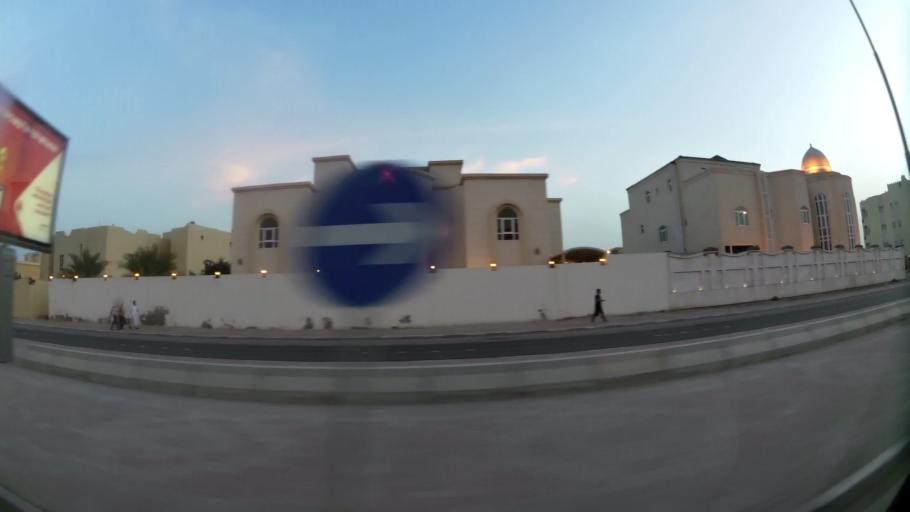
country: QA
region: Al Wakrah
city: Al Wakrah
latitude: 25.1619
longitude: 51.6046
